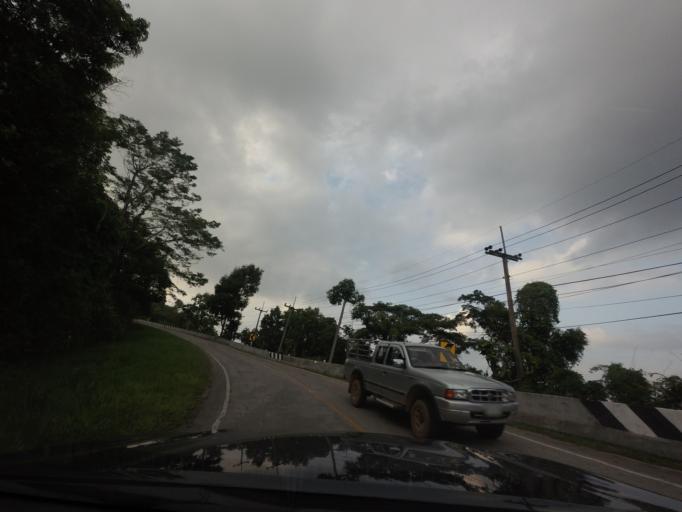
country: TH
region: Loei
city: Dan Sai
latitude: 17.3413
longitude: 101.0823
